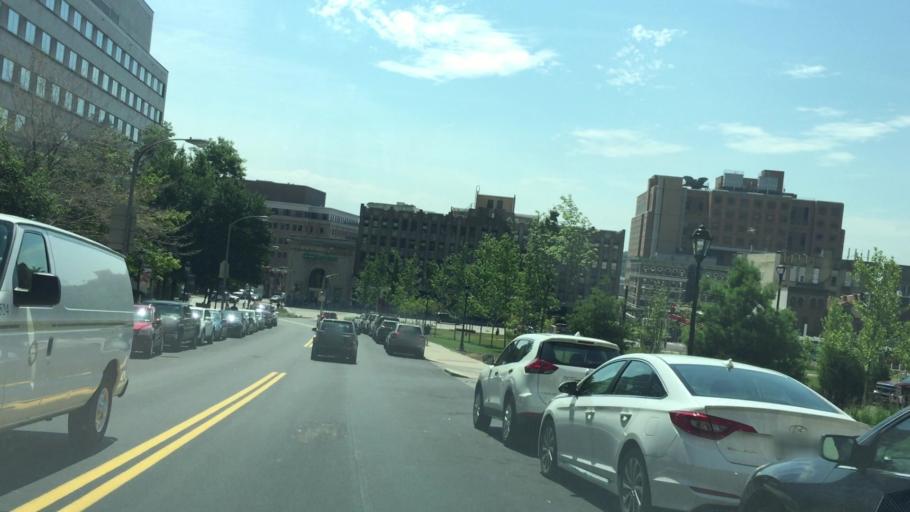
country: US
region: Pennsylvania
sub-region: Allegheny County
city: Bloomfield
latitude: 40.4429
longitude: -79.9596
